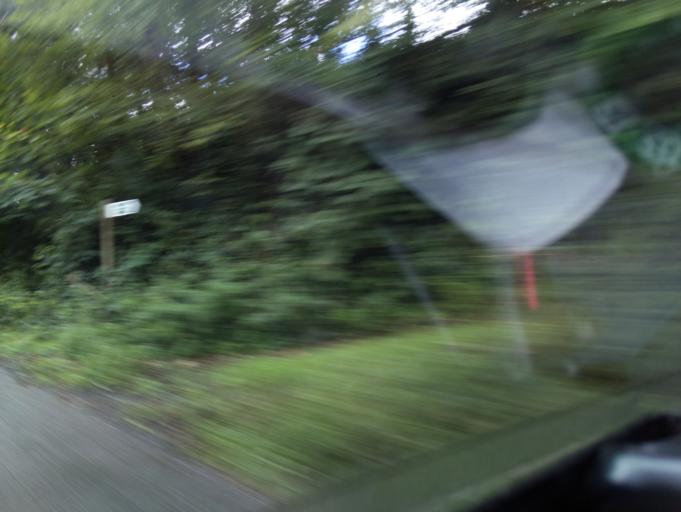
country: GB
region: England
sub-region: Devon
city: Modbury
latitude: 50.3369
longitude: -3.8558
